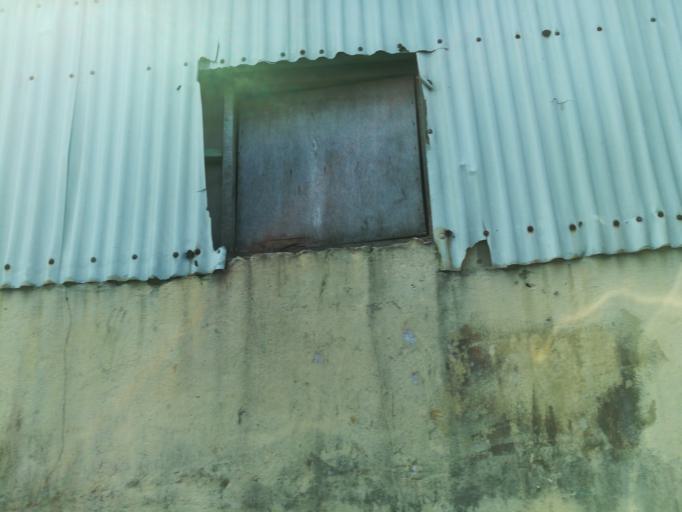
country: NG
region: Rivers
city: Port Harcourt
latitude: 4.8308
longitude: 6.9850
